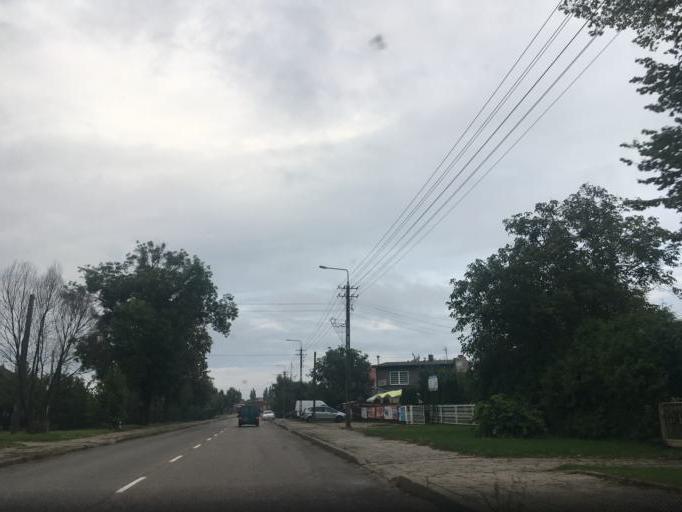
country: PL
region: Podlasie
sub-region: Powiat hajnowski
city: Hajnowka
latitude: 52.7417
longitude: 23.5696
